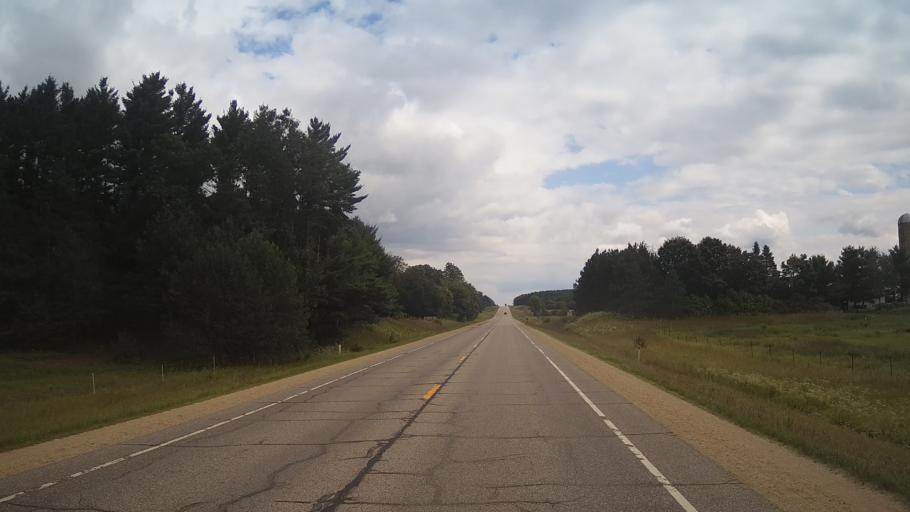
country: US
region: Wisconsin
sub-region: Marquette County
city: Westfield
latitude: 44.0380
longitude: -89.5010
